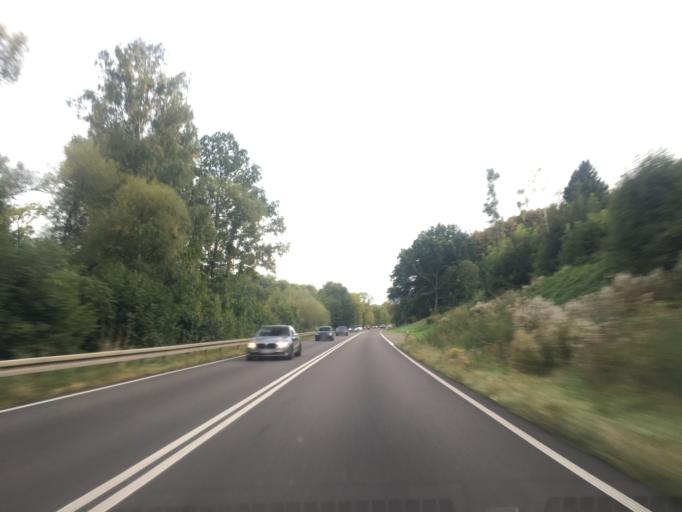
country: DE
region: Baden-Wuerttemberg
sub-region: Regierungsbezirk Stuttgart
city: Bempflingen
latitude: 48.5682
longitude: 9.2621
